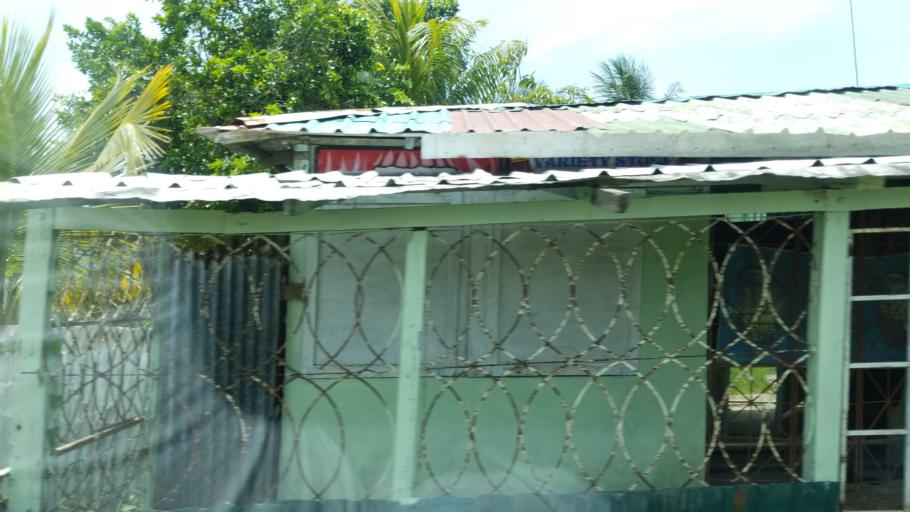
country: GY
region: Demerara-Mahaica
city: Georgetown
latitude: 6.7918
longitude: -58.1219
